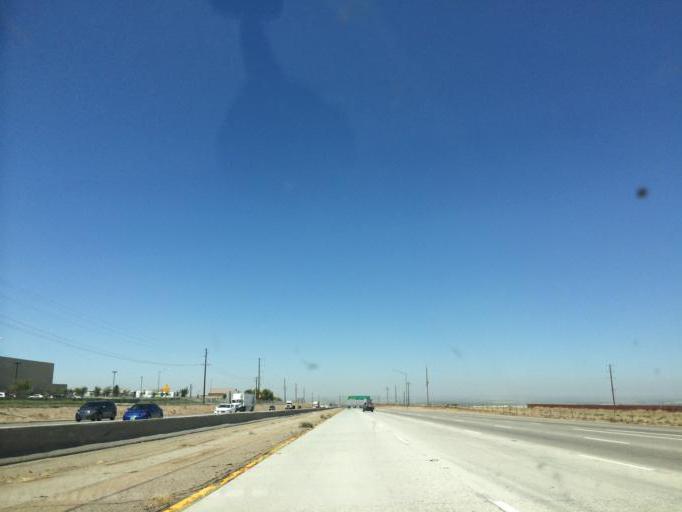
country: US
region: California
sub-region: Kern County
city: Frazier Park
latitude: 34.9904
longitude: -118.9465
